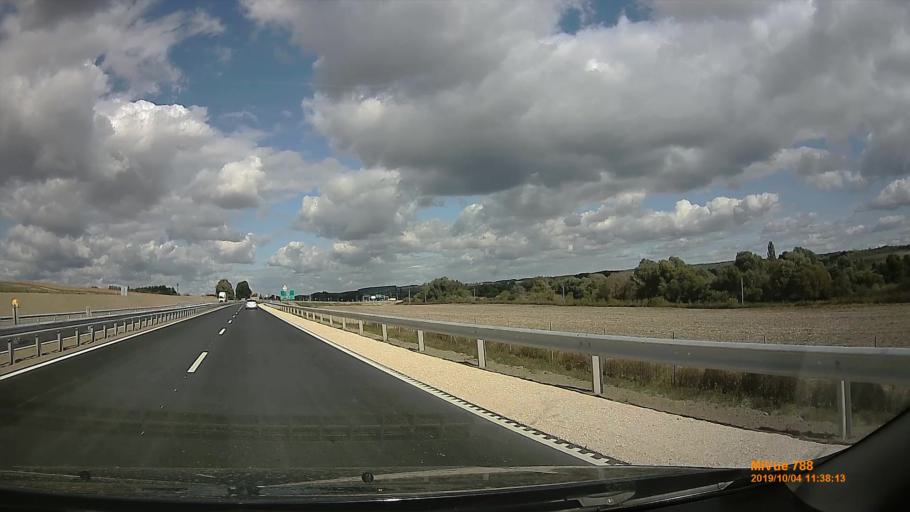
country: HU
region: Somogy
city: Karad
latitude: 46.5450
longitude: 17.8143
